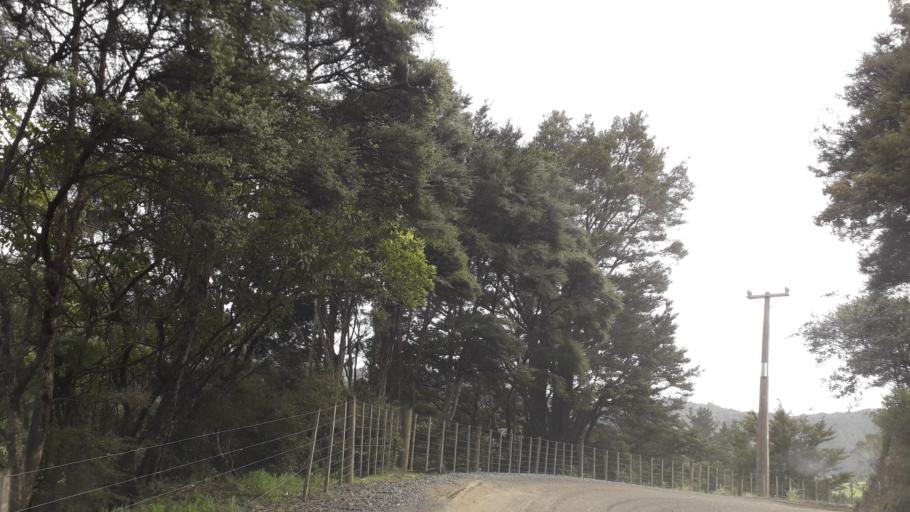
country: NZ
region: Northland
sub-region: Far North District
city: Kaitaia
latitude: -35.2307
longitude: 173.2645
